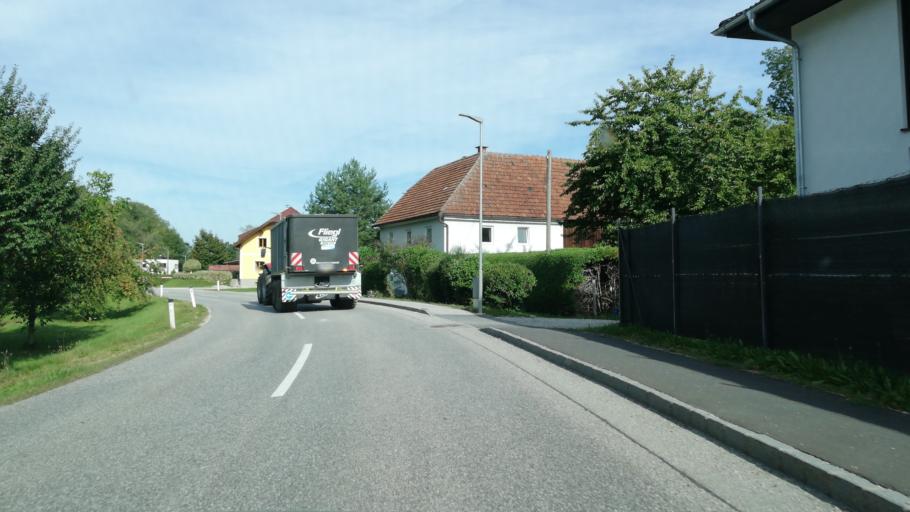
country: AT
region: Lower Austria
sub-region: Politischer Bezirk Amstetten
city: Behamberg
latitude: 48.0172
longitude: 14.4849
